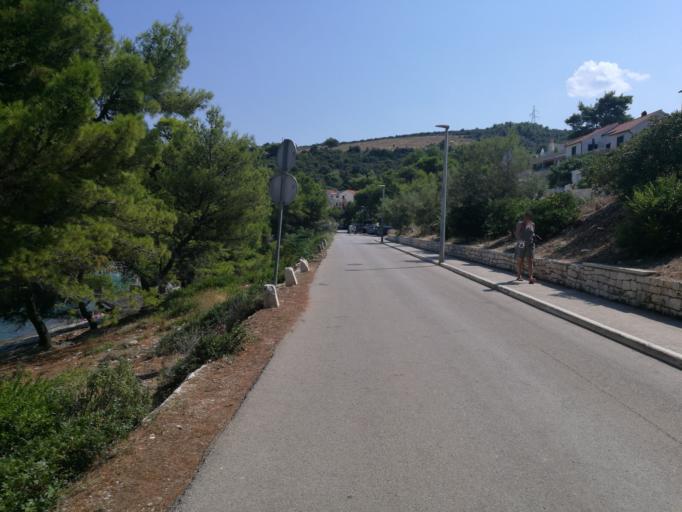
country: HR
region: Splitsko-Dalmatinska
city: Postira
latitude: 43.3759
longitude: 16.6380
